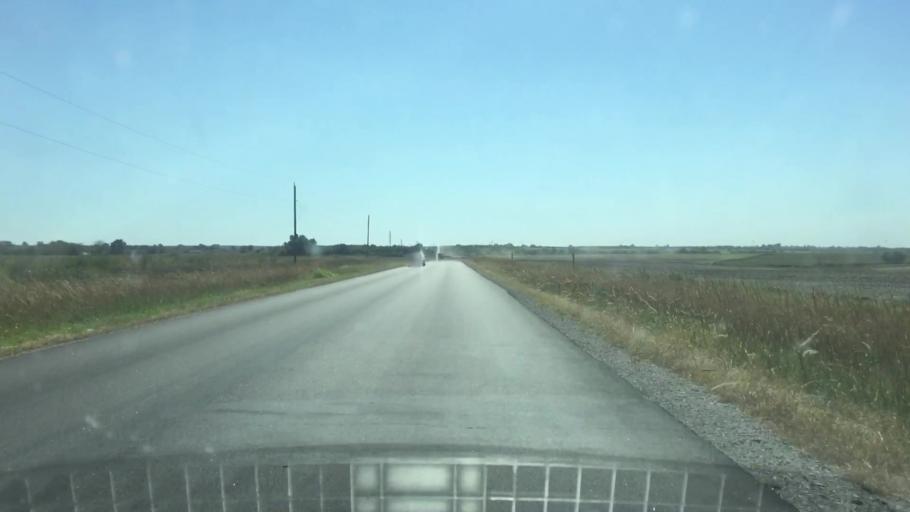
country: US
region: Kansas
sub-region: Marshall County
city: Marysville
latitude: 39.9484
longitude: -96.6008
